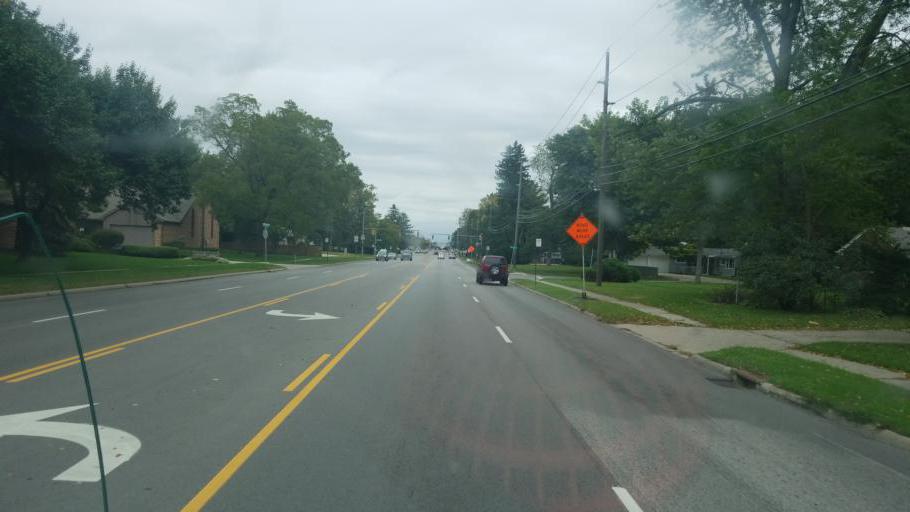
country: US
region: Ohio
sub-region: Lucas County
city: Ottawa Hills
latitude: 41.6772
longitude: -83.6337
